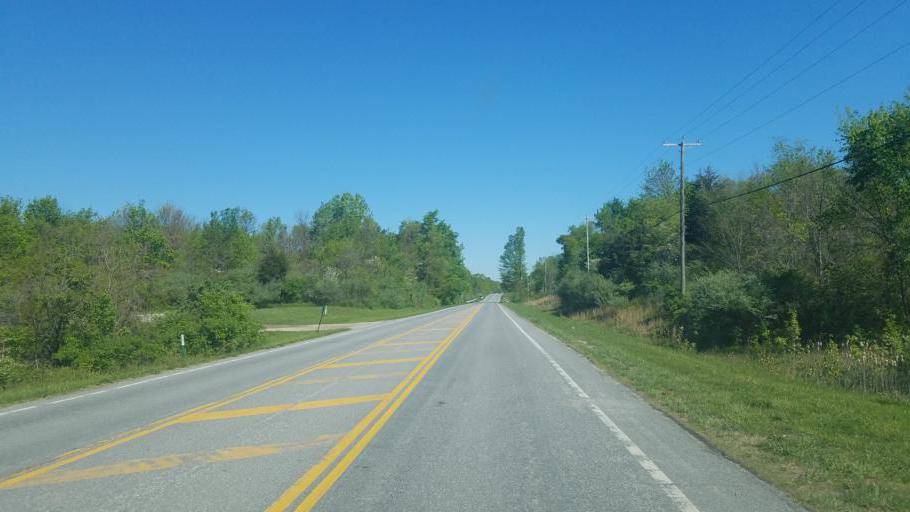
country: US
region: Ohio
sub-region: Delaware County
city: Lewis Center
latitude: 40.2260
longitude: -82.9572
